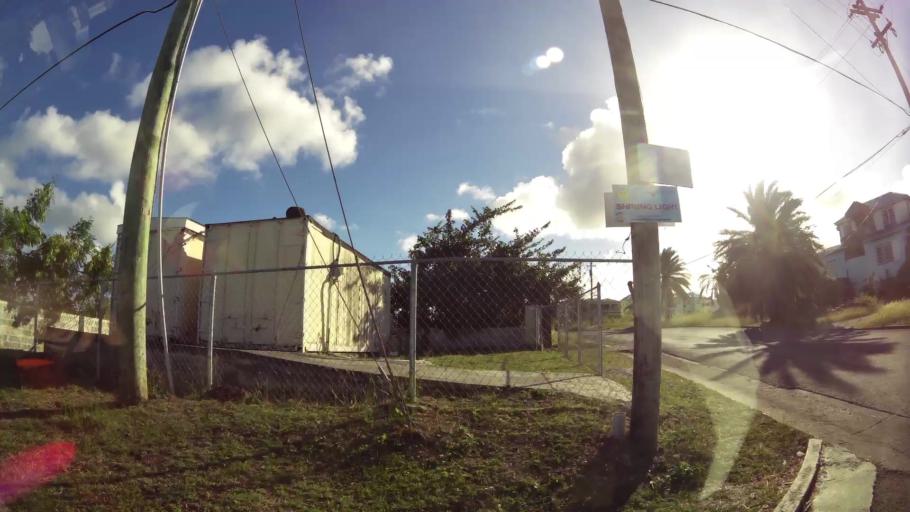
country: AG
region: Saint John
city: Potters Village
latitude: 17.0939
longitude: -61.8024
